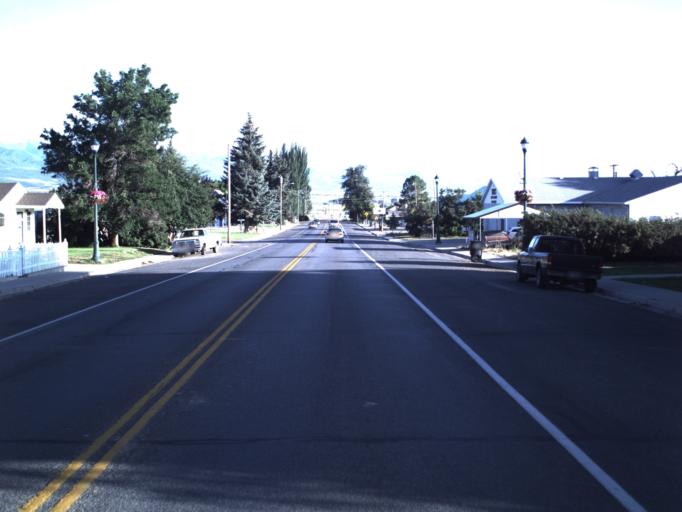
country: US
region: Utah
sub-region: Sanpete County
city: Fairview
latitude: 39.6259
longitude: -111.4393
